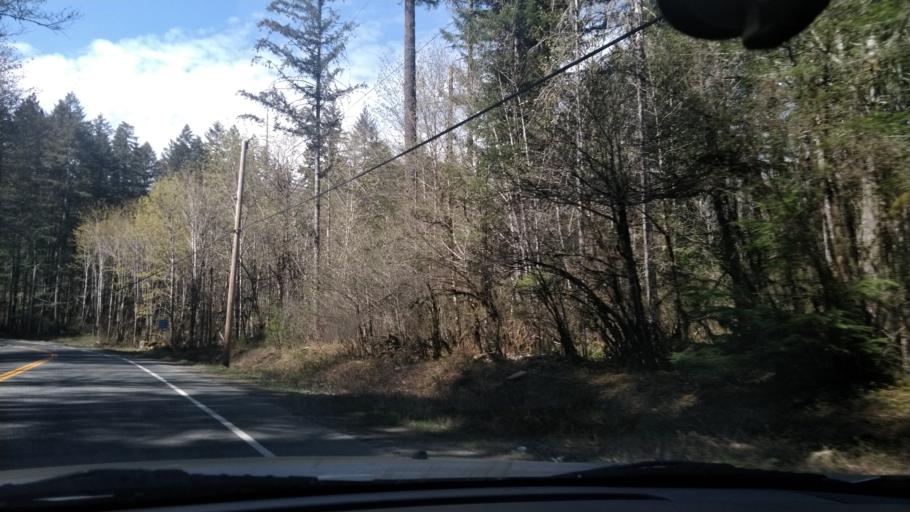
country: CA
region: British Columbia
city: Courtenay
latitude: 49.6952
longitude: -125.0563
